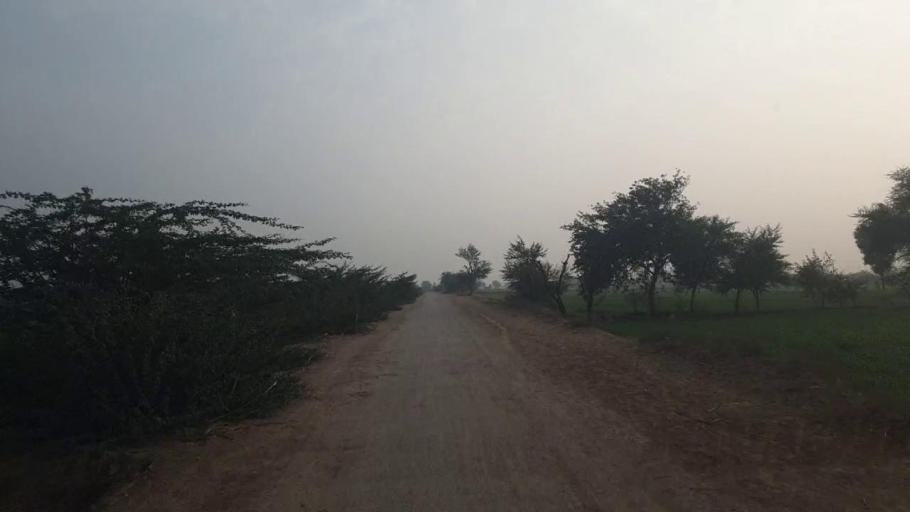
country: PK
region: Sindh
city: Berani
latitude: 25.8060
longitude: 68.7497
